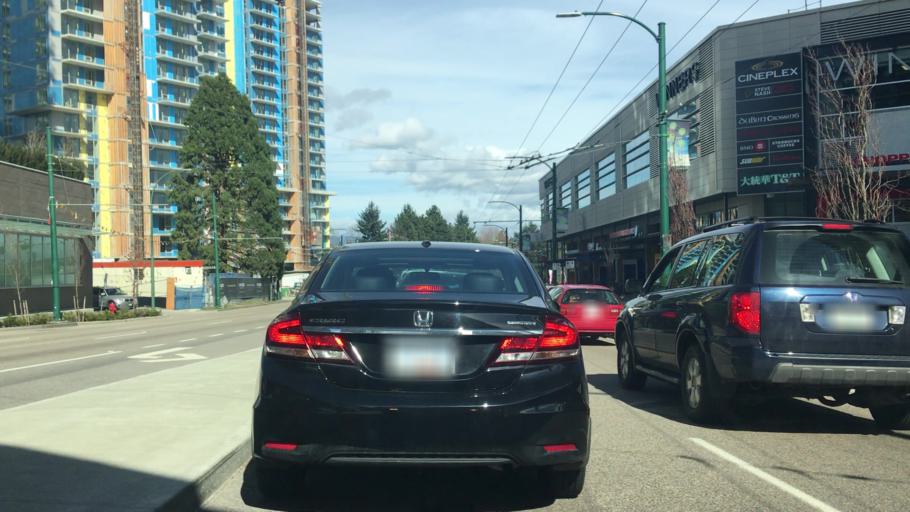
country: CA
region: British Columbia
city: Vancouver
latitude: 49.2101
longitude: -123.1168
